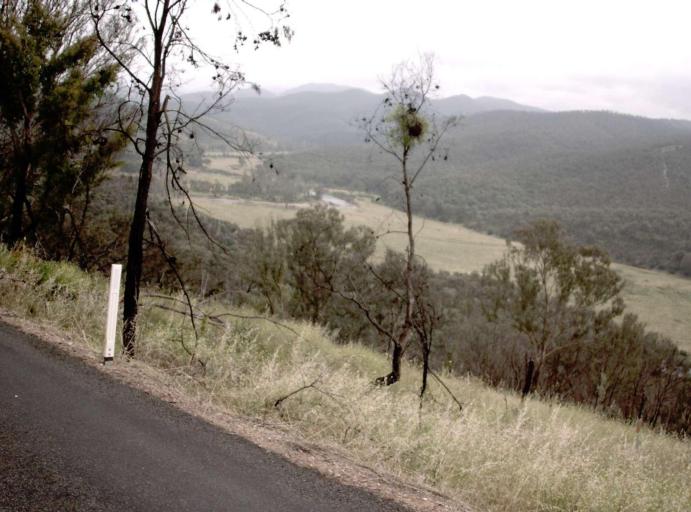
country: AU
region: Victoria
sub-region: Wellington
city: Heyfield
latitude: -37.8200
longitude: 146.6748
